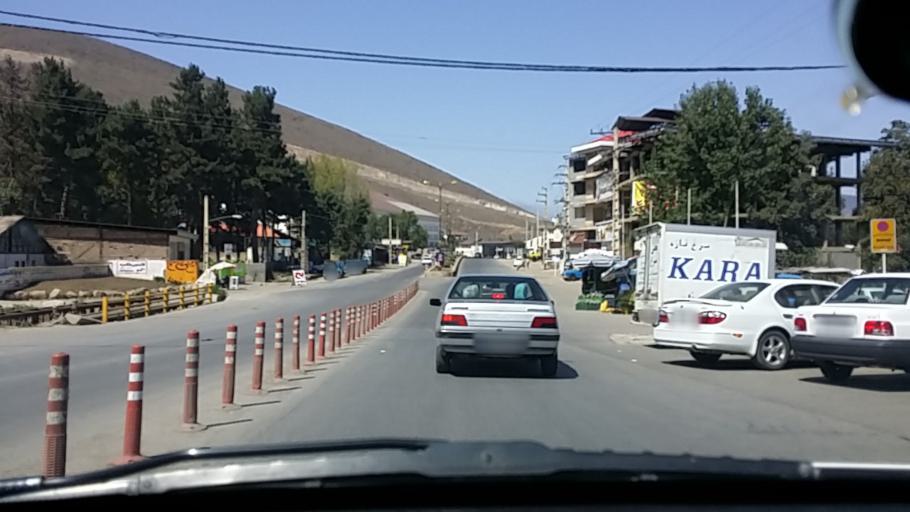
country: IR
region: Mazandaran
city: `Abbasabad
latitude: 36.5067
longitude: 51.1586
